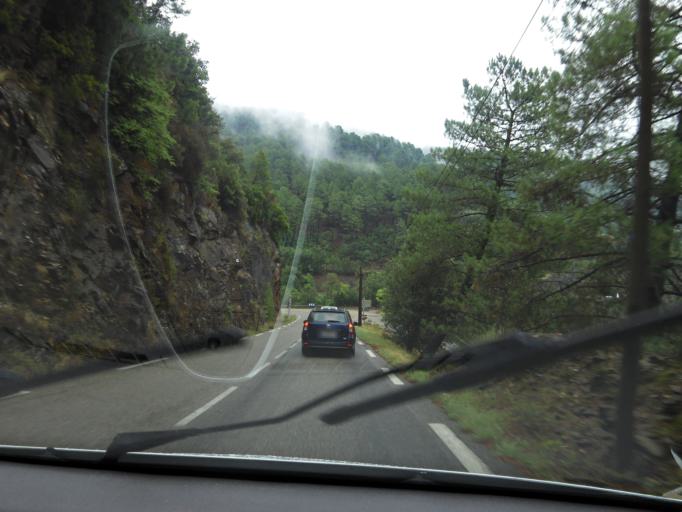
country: FR
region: Languedoc-Roussillon
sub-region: Departement du Gard
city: Branoux-les-Taillades
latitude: 44.2441
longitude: 3.9832
